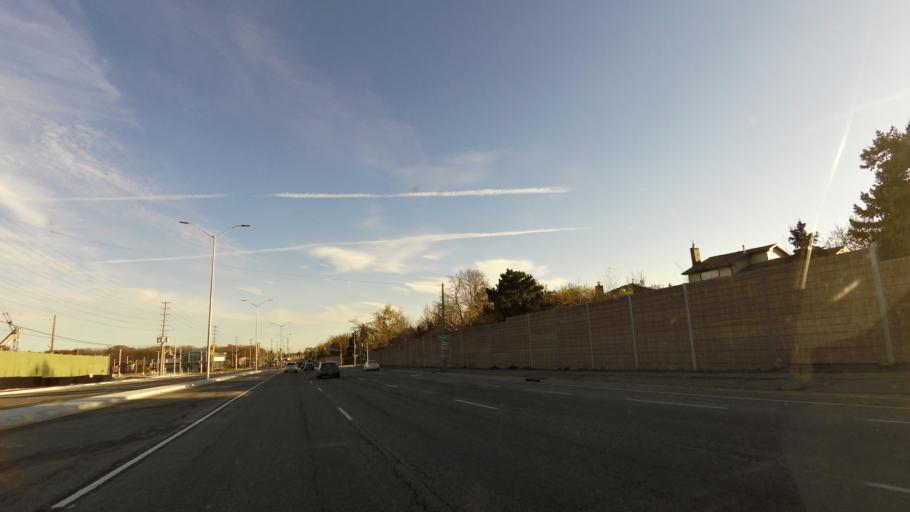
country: CA
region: Ontario
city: Mississauga
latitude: 43.5813
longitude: -79.7373
